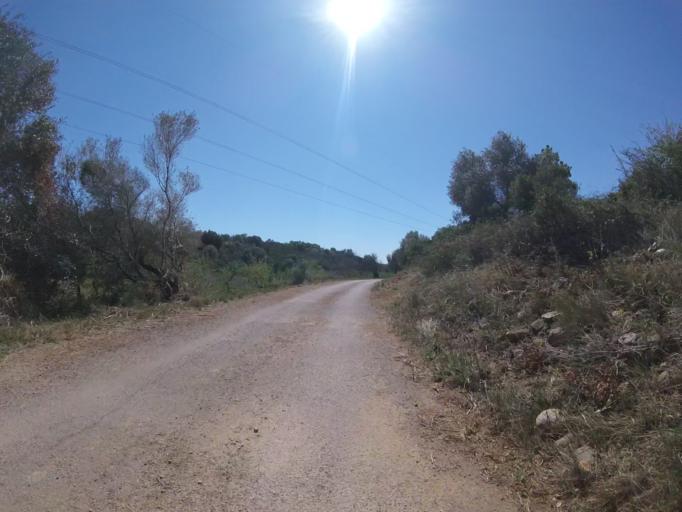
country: ES
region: Valencia
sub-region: Provincia de Castello
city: Cuevas de Vinroma
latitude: 40.3733
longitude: 0.1346
